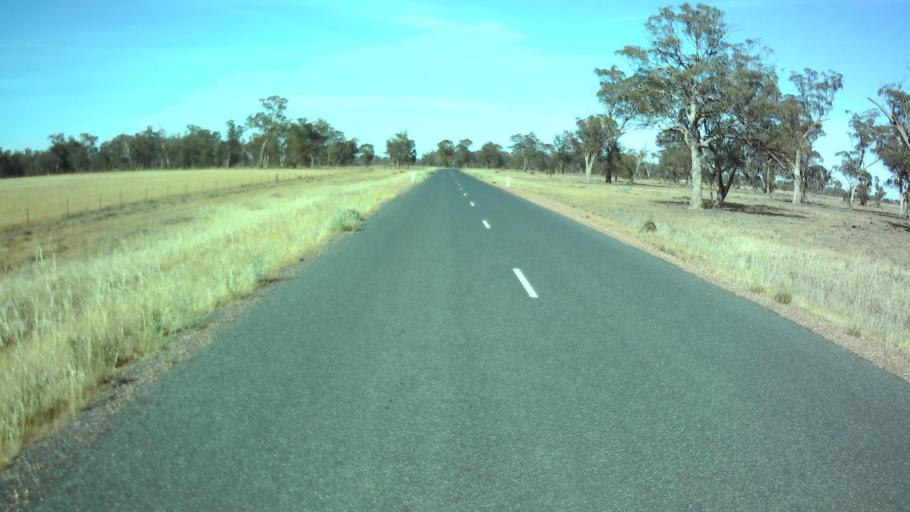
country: AU
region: New South Wales
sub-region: Weddin
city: Grenfell
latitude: -34.1108
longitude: 147.8519
